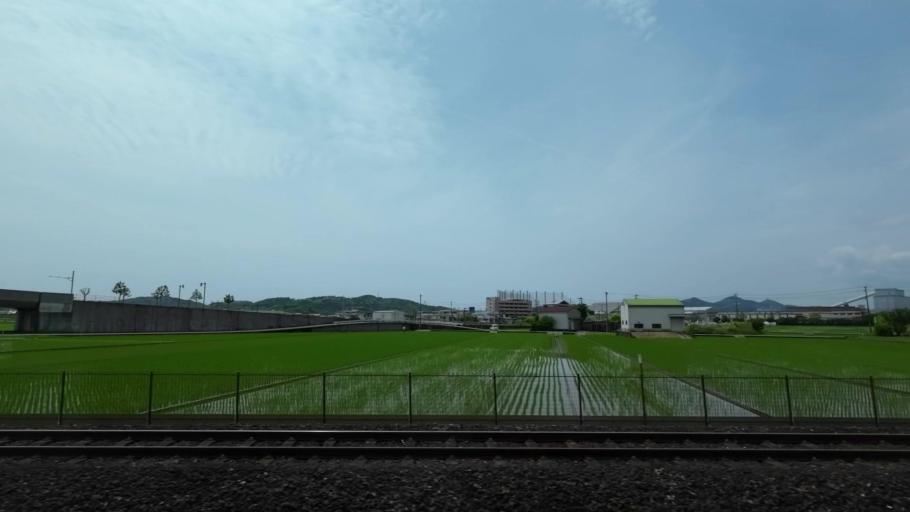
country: JP
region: Kochi
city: Kochi-shi
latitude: 33.5778
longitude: 133.5804
